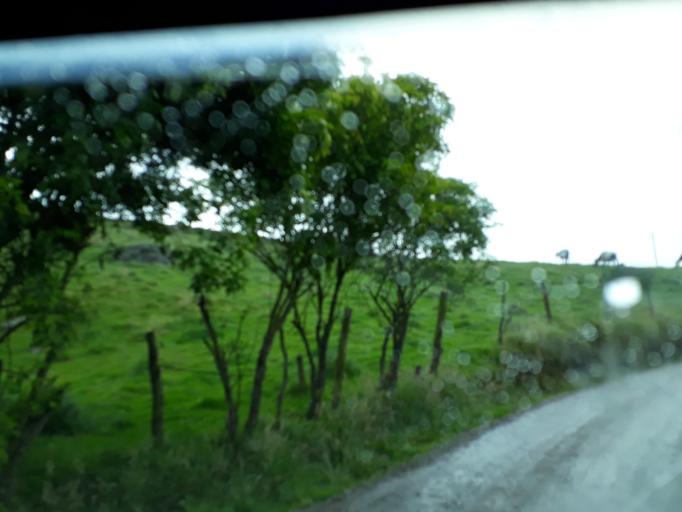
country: CO
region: Cundinamarca
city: La Mesa
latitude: 5.1696
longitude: -73.9145
